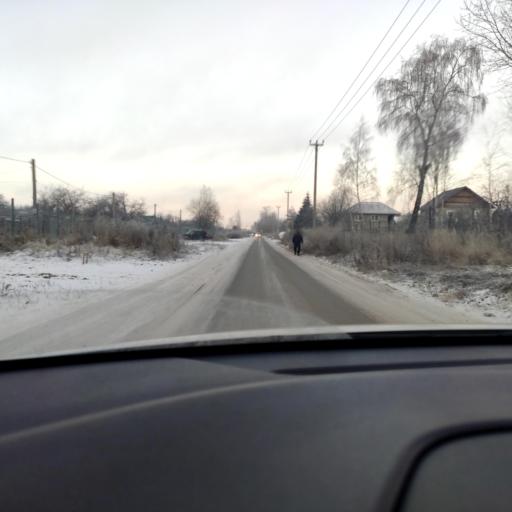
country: RU
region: Tatarstan
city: Staroye Arakchino
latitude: 55.8606
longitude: 49.0525
